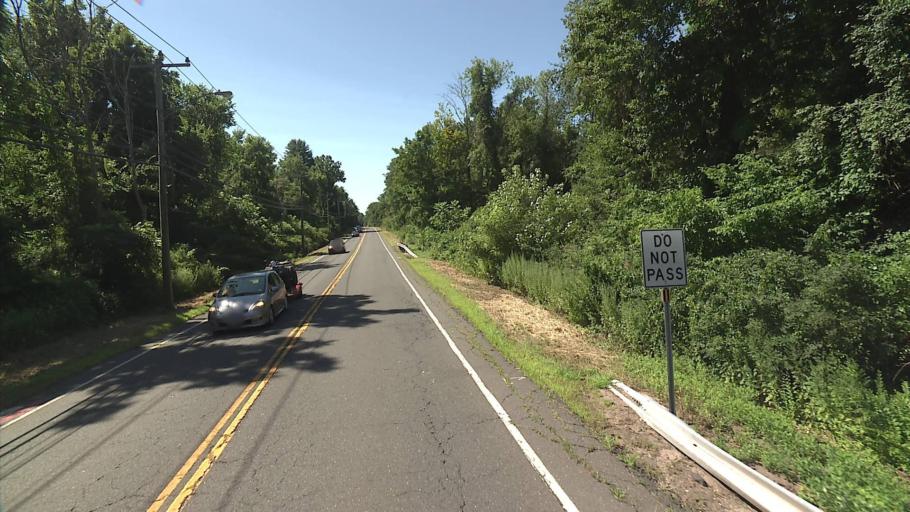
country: US
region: Connecticut
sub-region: Hartford County
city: Farmington
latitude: 41.7528
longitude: -72.8189
